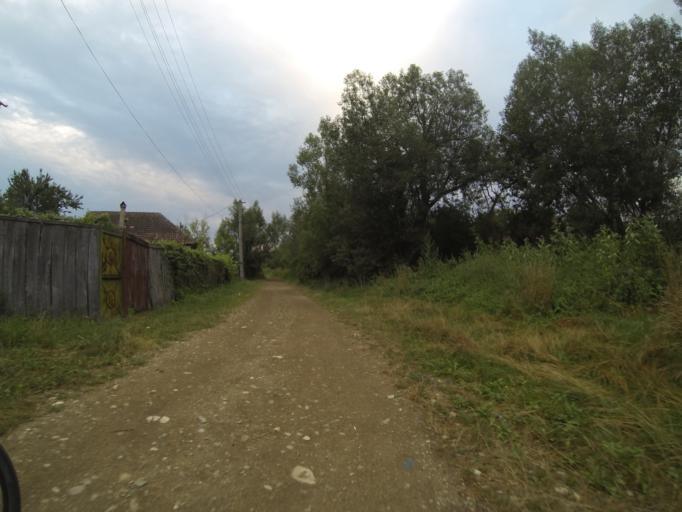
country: RO
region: Brasov
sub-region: Comuna Sinca Veche
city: Sinca Veche
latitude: 45.7625
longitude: 25.1757
